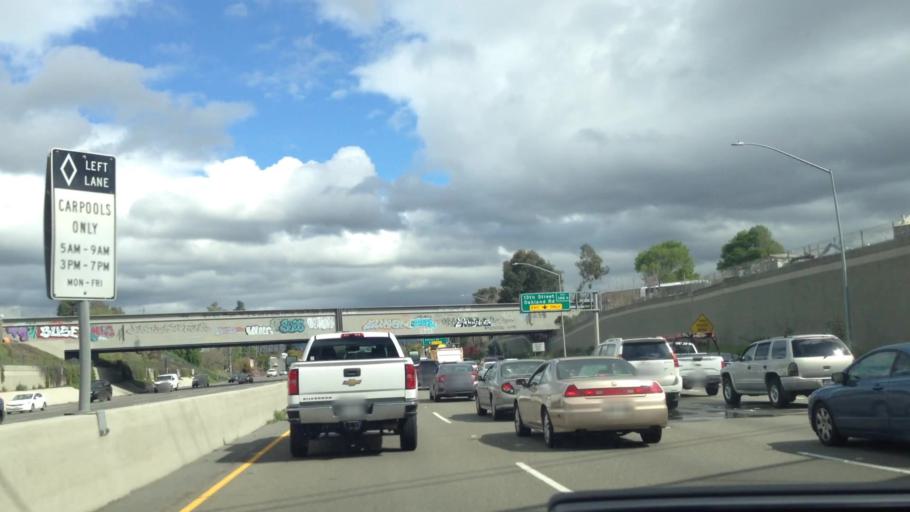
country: US
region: California
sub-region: Santa Clara County
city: San Jose
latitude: 37.3634
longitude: -121.8989
